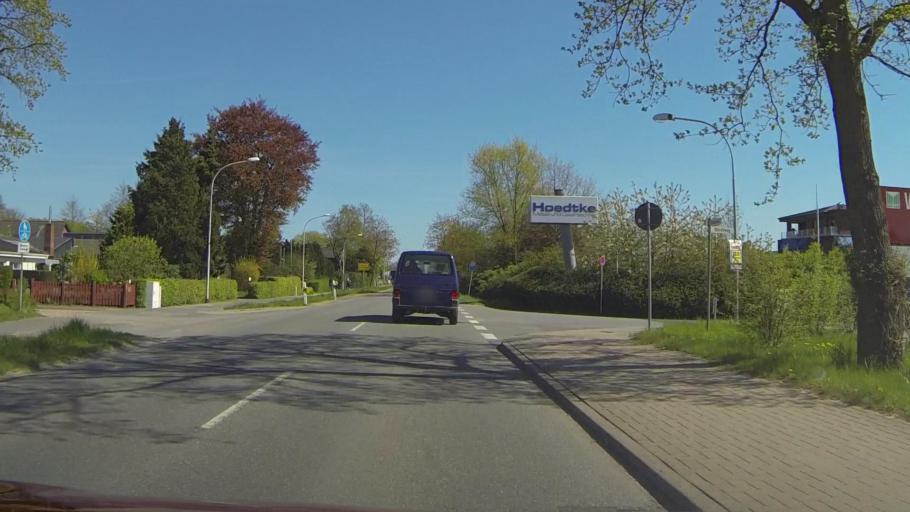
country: DE
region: Schleswig-Holstein
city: Kummerfeld
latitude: 53.6720
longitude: 9.7752
